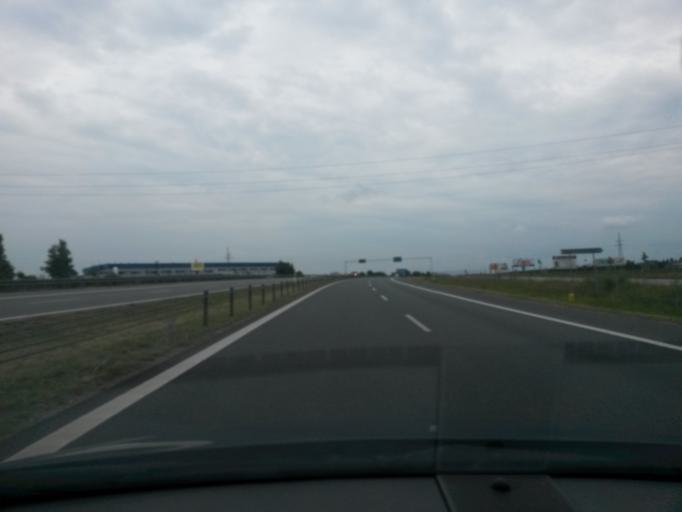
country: PL
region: Masovian Voivodeship
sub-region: Powiat zyrardowski
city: Mszczonow
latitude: 51.9866
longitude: 20.5364
